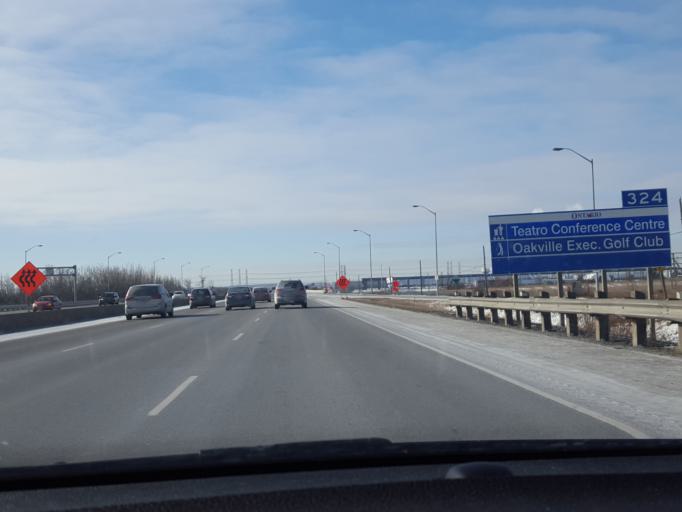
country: CA
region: Ontario
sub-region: Halton
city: Milton
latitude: 43.5561
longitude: -79.8464
